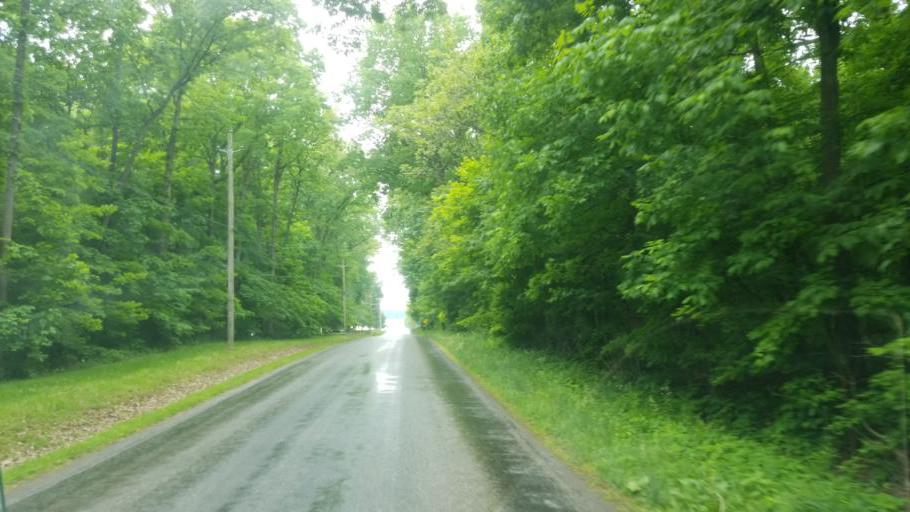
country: US
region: Ohio
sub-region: Wayne County
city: Apple Creek
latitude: 40.7778
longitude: -81.8016
